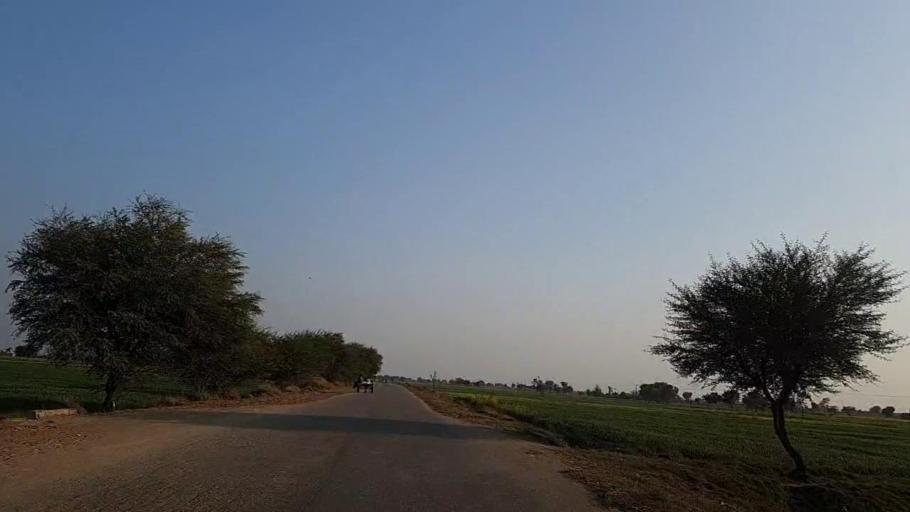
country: PK
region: Sindh
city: Sakrand
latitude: 26.0540
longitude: 68.4137
